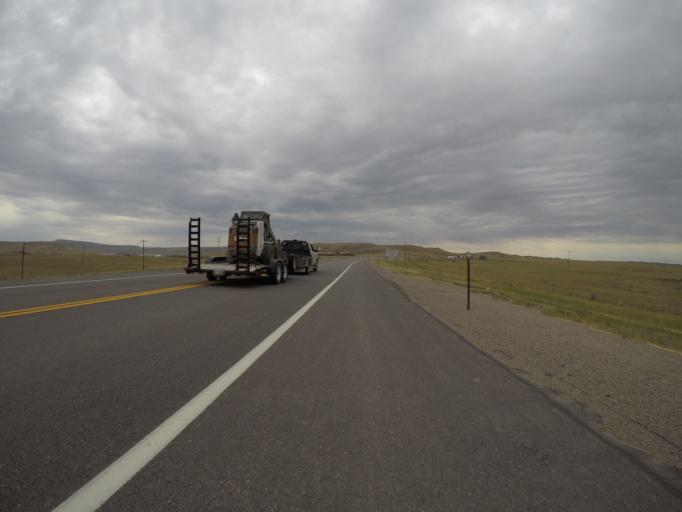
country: US
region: Wyoming
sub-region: Lincoln County
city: Kemmerer
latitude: 41.7939
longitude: -110.5814
